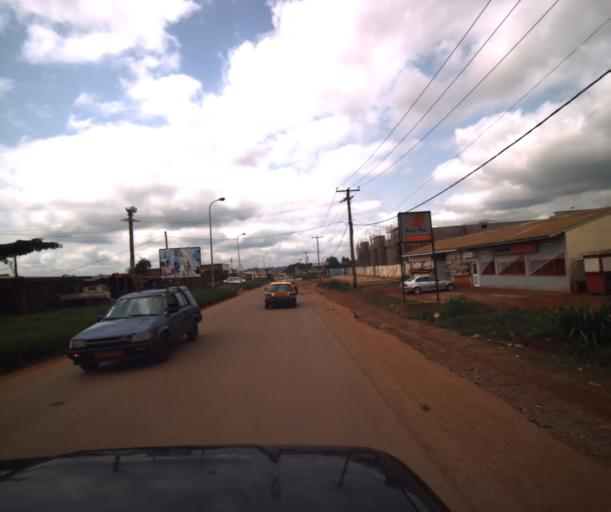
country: CM
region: Centre
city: Yaounde
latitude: 3.8166
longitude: 11.5130
